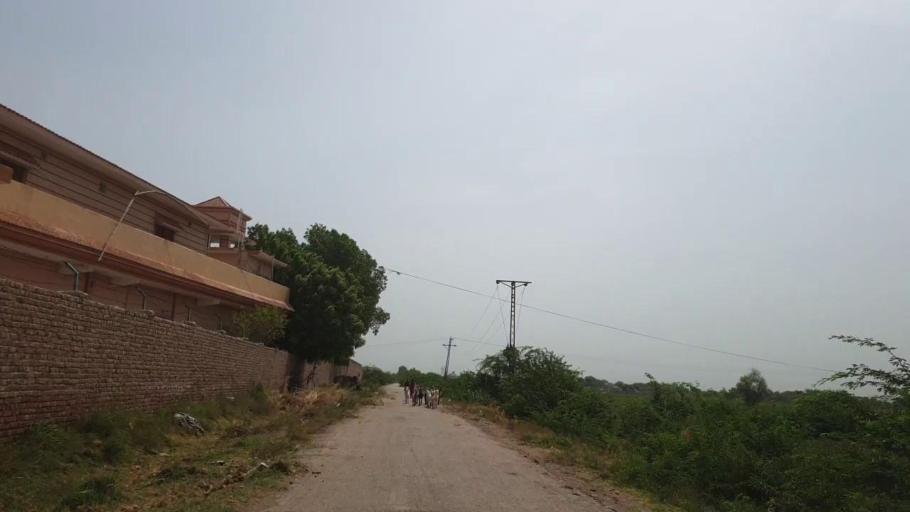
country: PK
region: Sindh
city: Sakrand
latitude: 26.1143
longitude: 68.2901
